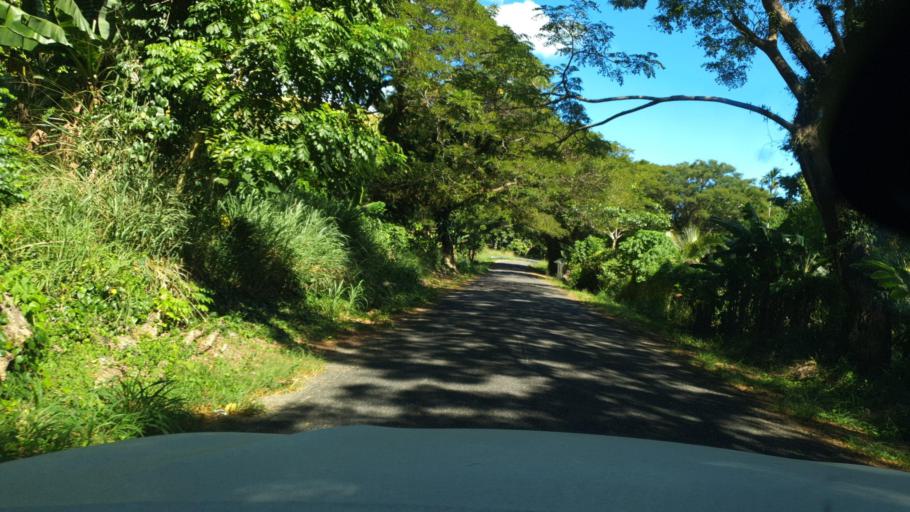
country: SB
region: Guadalcanal
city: Honiara
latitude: -9.2534
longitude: 159.6973
